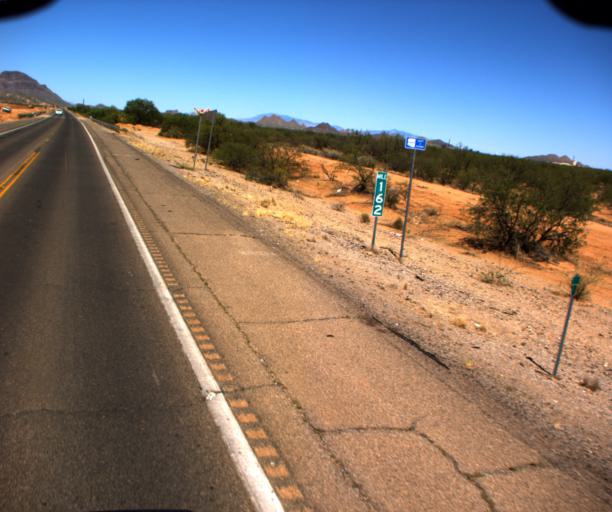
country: US
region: Arizona
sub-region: Pima County
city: Valencia West
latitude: 32.1451
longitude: -111.1372
